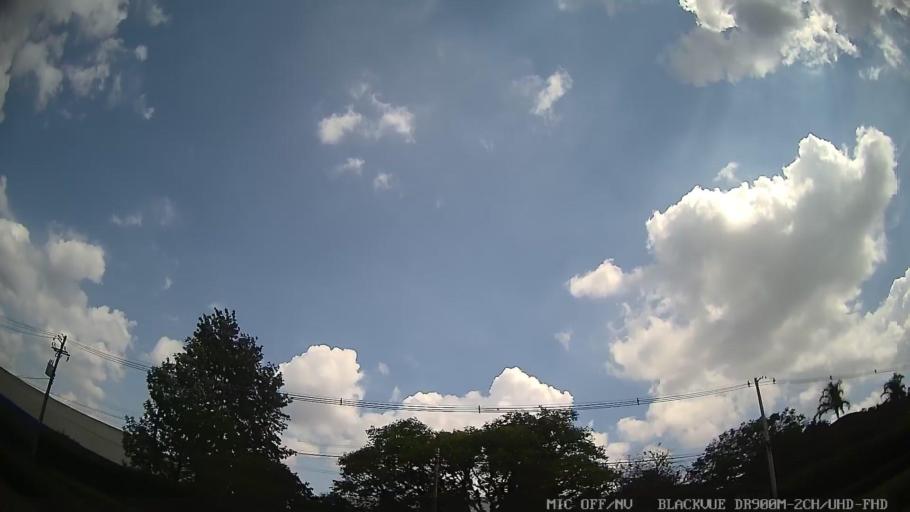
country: BR
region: Sao Paulo
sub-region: Itatiba
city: Itatiba
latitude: -22.9806
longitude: -46.7411
